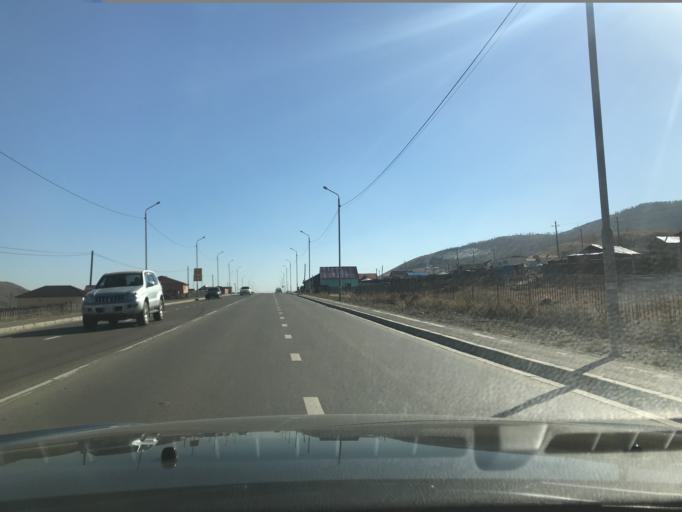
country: MN
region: Ulaanbaatar
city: Ulaanbaatar
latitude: 48.0418
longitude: 106.9039
